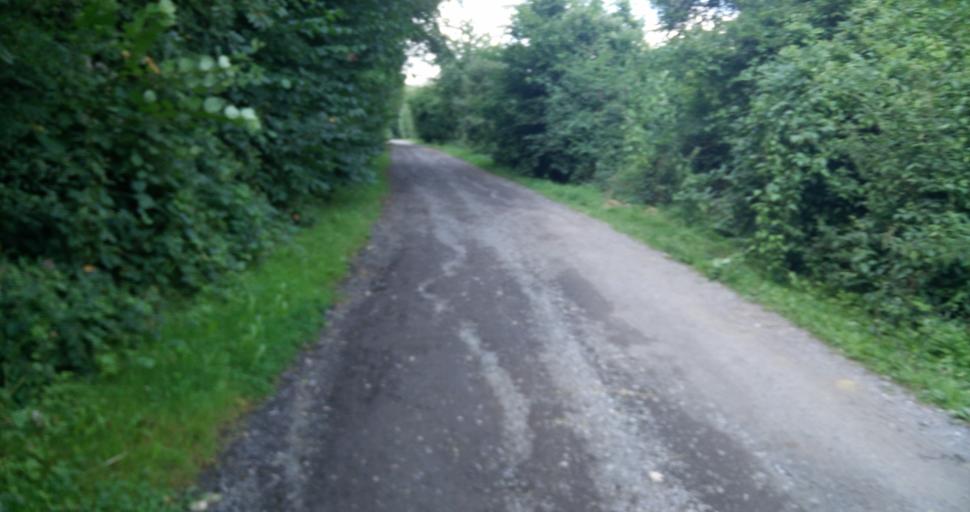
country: BE
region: Wallonia
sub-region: Province de Liege
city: Vise
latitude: 50.7418
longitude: 5.7252
